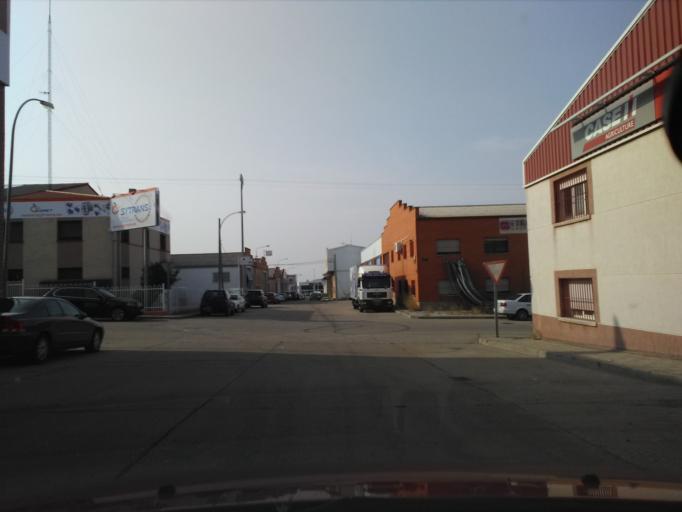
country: ES
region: Castille and Leon
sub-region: Provincia de Salamanca
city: Villares de la Reina
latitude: 40.9898
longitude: -5.6399
